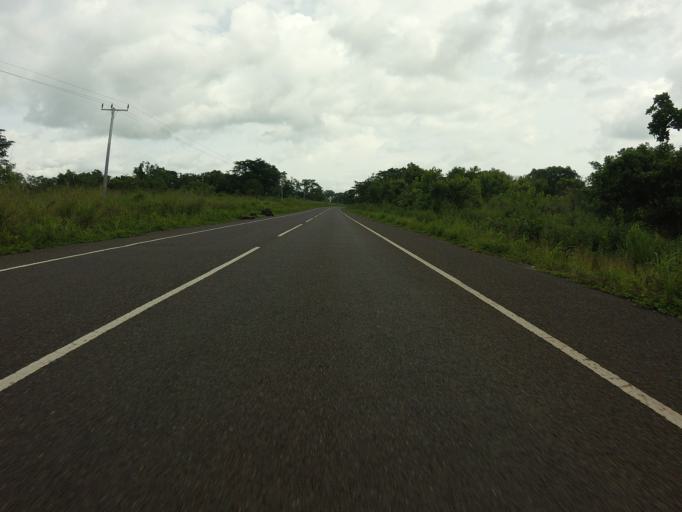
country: TG
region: Plateaux
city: Badou
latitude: 7.9835
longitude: 0.5605
